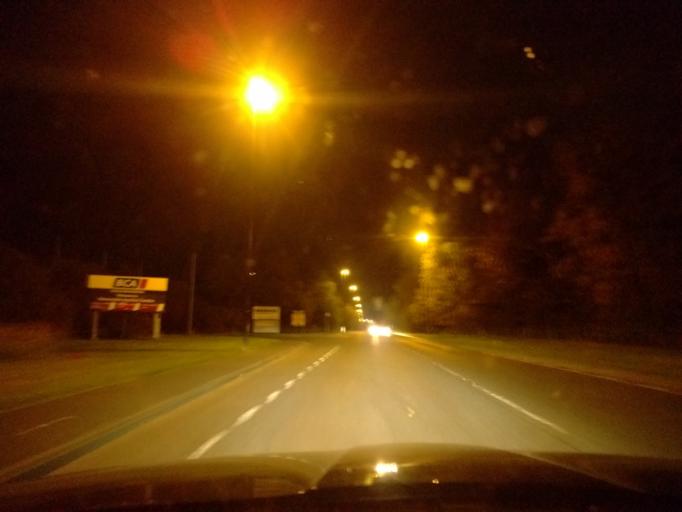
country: GB
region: England
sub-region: Borough of North Tyneside
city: Wallsend
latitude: 55.0160
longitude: -1.5467
